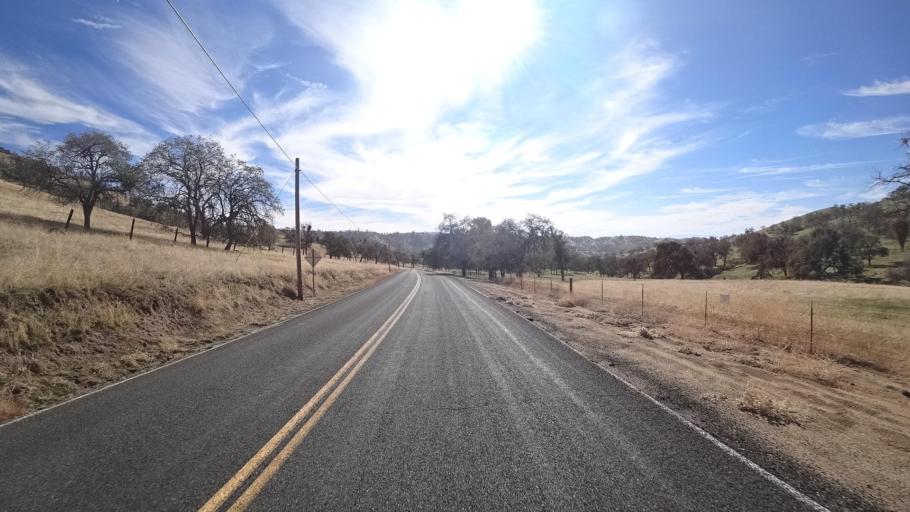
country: US
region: California
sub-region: Kern County
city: Alta Sierra
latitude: 35.6350
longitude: -118.8014
